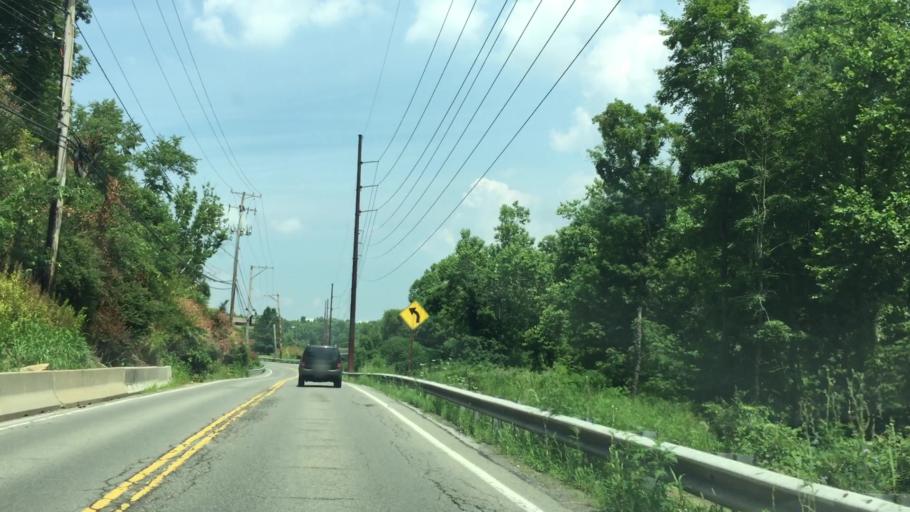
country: US
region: Pennsylvania
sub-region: Allegheny County
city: Enlow
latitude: 40.4540
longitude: -80.1963
